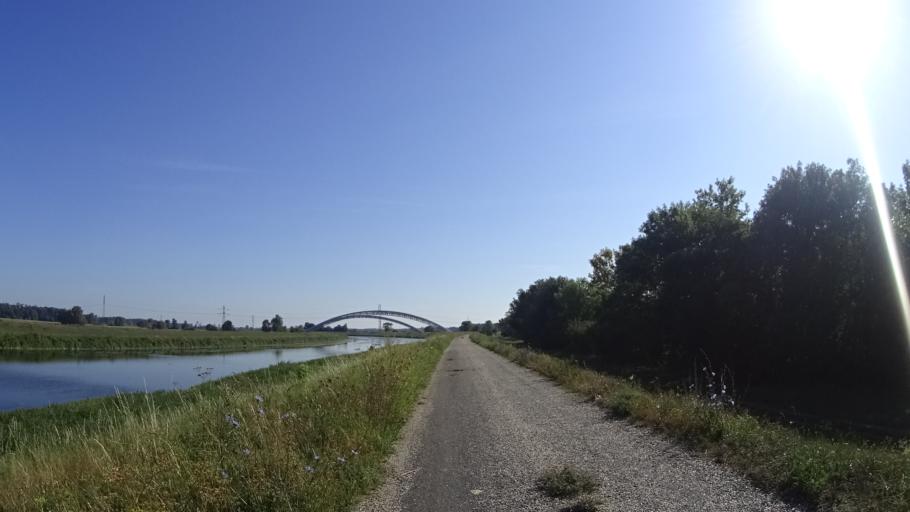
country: CZ
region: South Moravian
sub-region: Okres Breclav
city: Lanzhot
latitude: 48.7136
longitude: 17.0056
